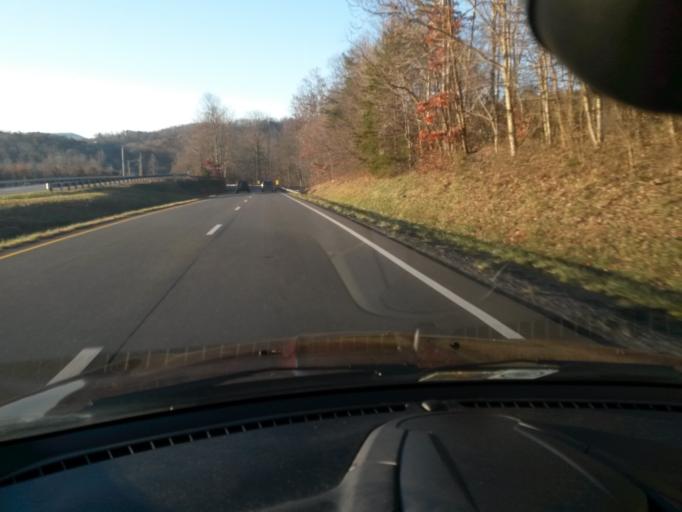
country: US
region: Virginia
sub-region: Franklin County
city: Henry Fork
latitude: 36.9095
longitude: -79.8661
